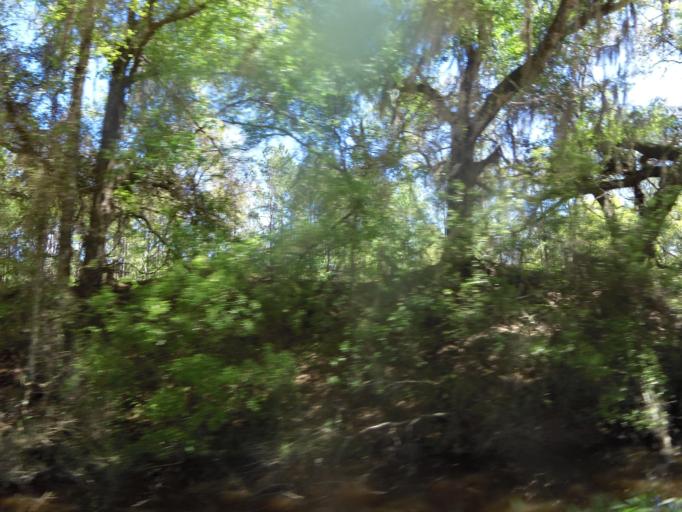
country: US
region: Florida
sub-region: Bradford County
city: Starke
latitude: 30.0497
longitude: -82.0533
